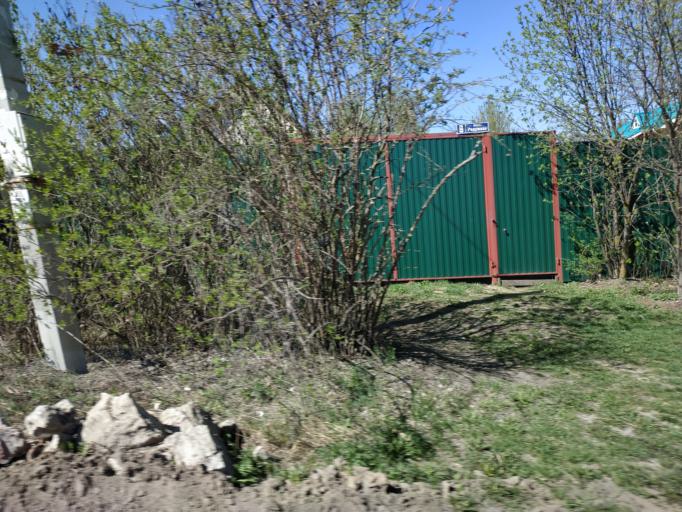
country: RU
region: Moskovskaya
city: Malyshevo
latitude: 55.4587
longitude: 38.3777
